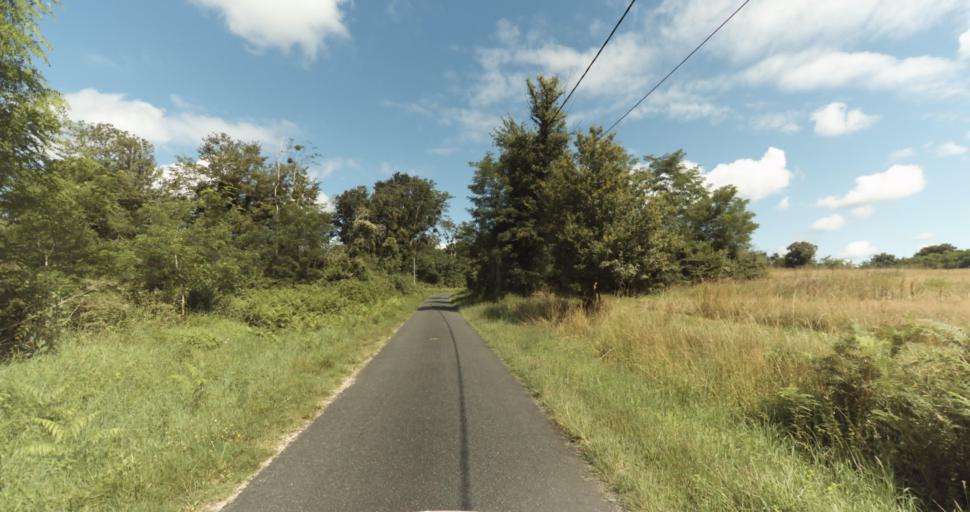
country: FR
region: Aquitaine
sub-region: Departement de la Gironde
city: Bazas
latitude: 44.4619
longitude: -0.2174
